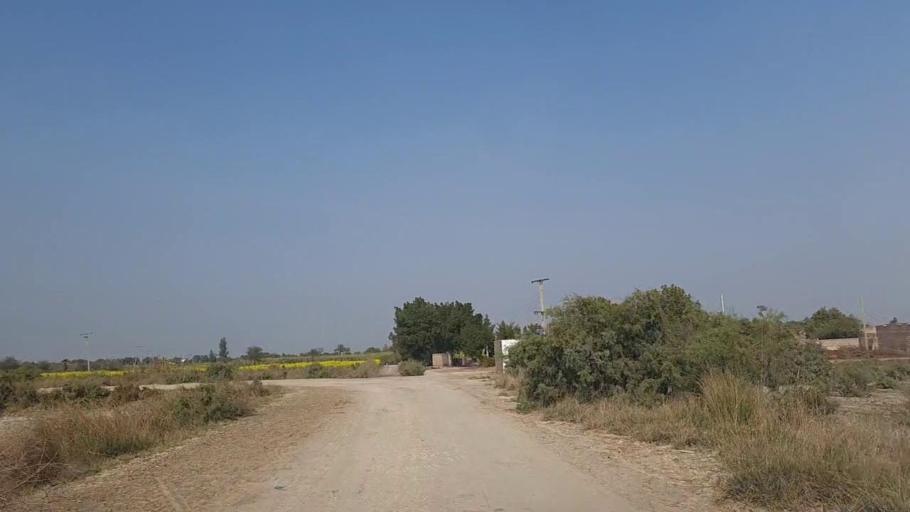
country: PK
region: Sindh
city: Daur
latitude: 26.4879
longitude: 68.4514
